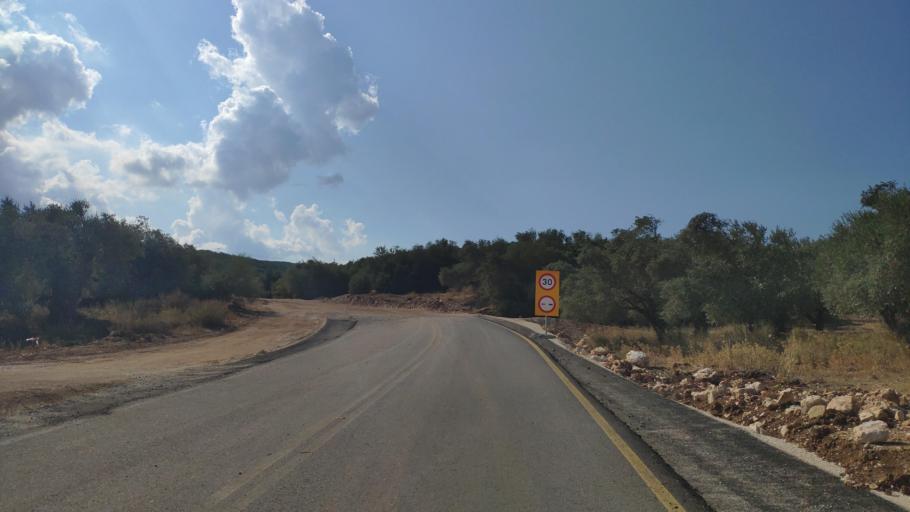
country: GR
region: West Greece
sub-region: Nomos Aitolias kai Akarnanias
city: Stanos
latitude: 38.7746
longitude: 21.1835
